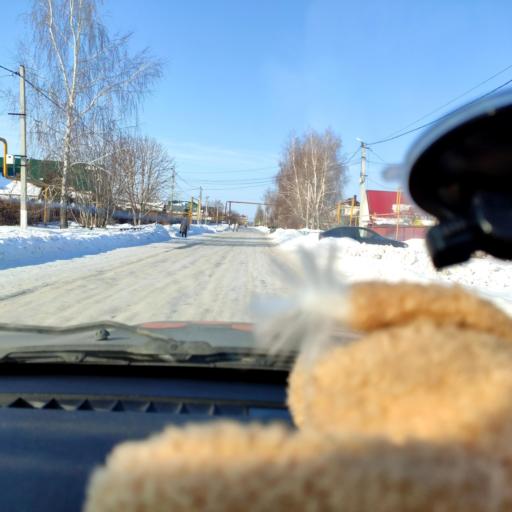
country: RU
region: Samara
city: Podstepki
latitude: 53.5137
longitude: 49.1218
